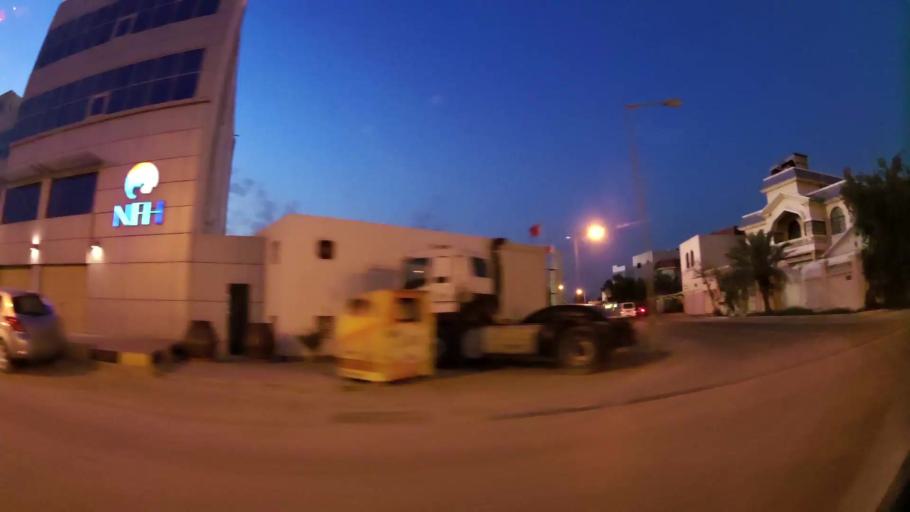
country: BH
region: Manama
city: Jidd Hafs
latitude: 26.2014
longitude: 50.5592
